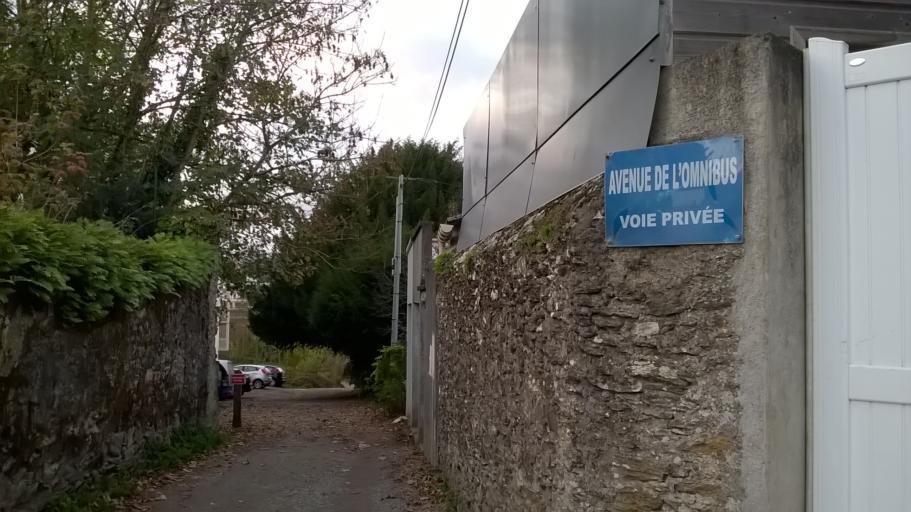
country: FR
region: Pays de la Loire
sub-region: Departement de la Loire-Atlantique
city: Nantes
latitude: 47.2314
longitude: -1.5455
